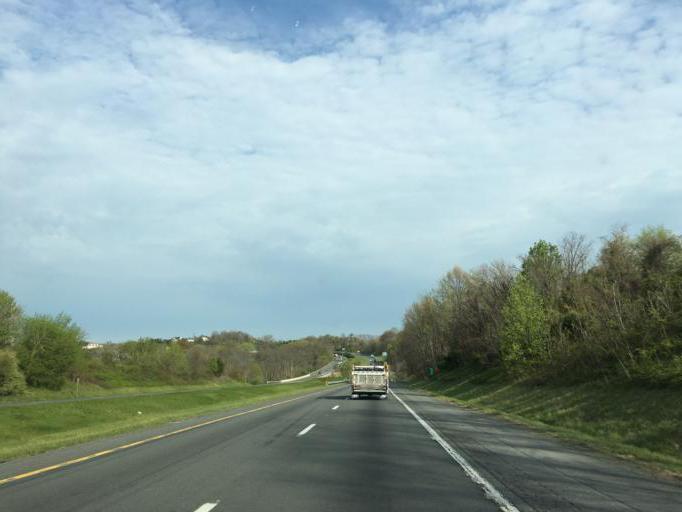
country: US
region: Maryland
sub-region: Frederick County
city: Middletown
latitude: 39.4785
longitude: -77.5364
